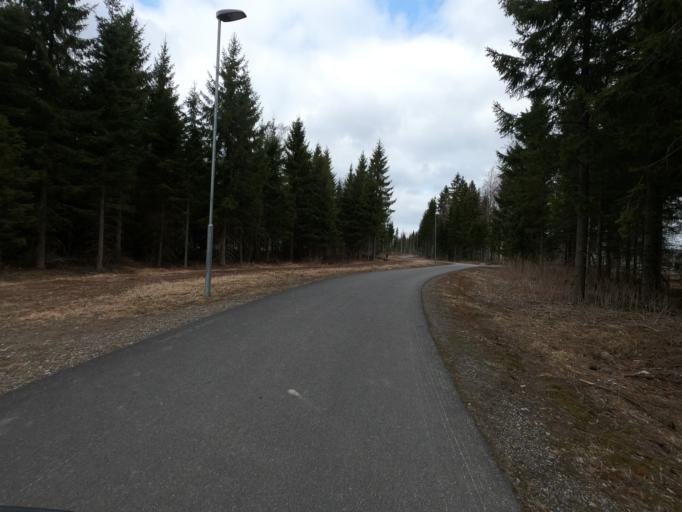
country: FI
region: North Karelia
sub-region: Joensuu
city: Joensuu
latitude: 62.5624
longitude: 29.8217
